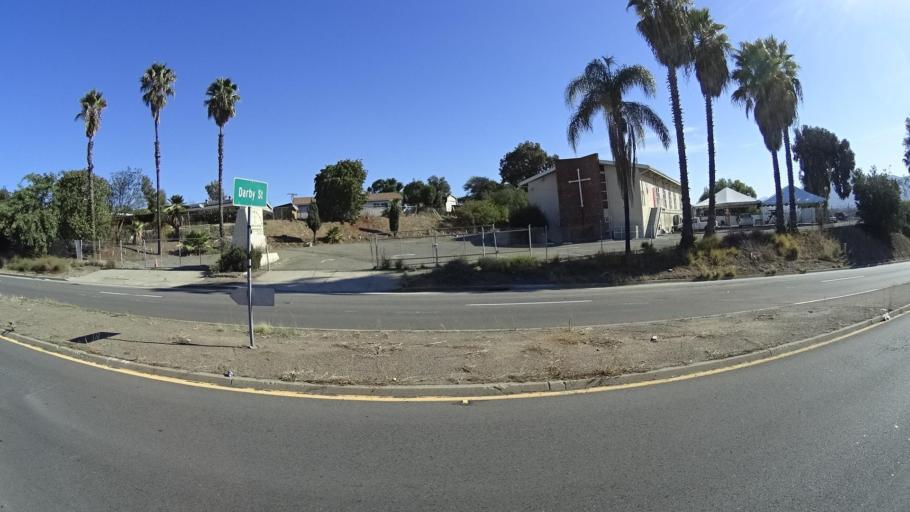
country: US
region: California
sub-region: San Diego County
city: La Presa
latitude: 32.7163
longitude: -117.0199
